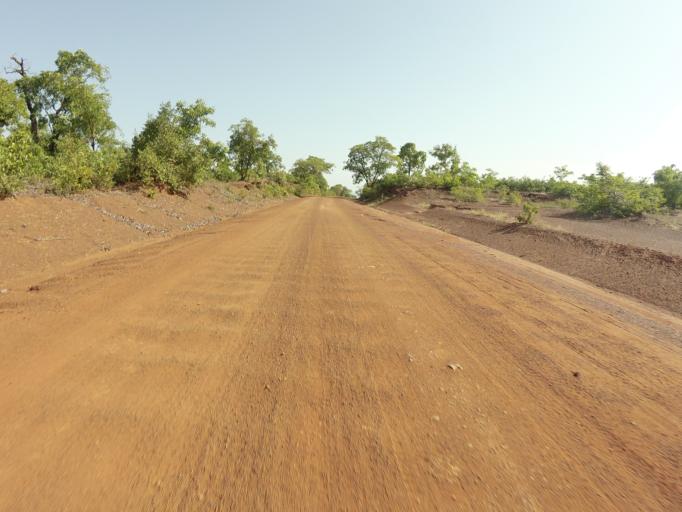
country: GH
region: Upper East
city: Bawku
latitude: 10.7366
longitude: -0.2020
